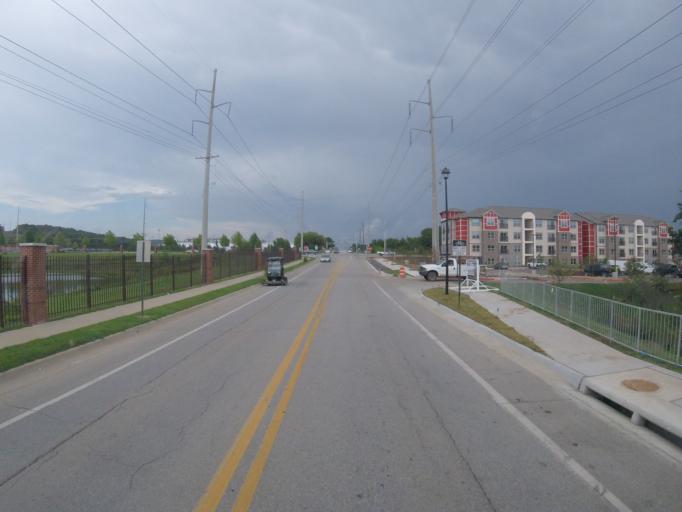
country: US
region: Arkansas
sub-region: Washington County
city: Fayetteville
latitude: 36.0487
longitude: -94.1822
